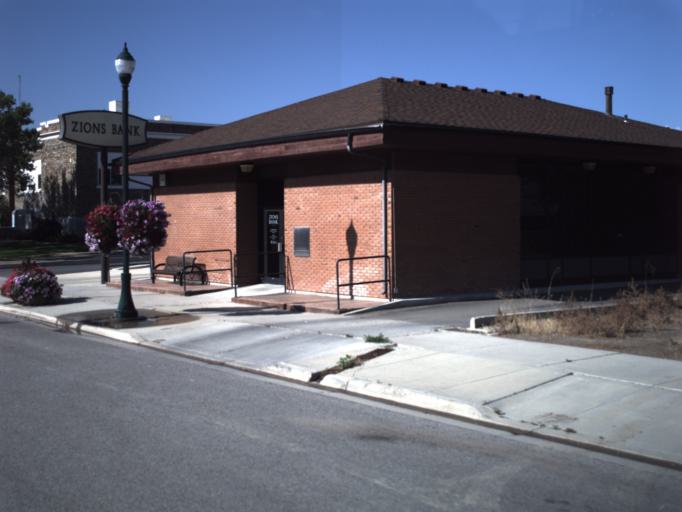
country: US
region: Utah
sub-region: Emery County
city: Huntington
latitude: 39.3276
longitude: -110.9647
